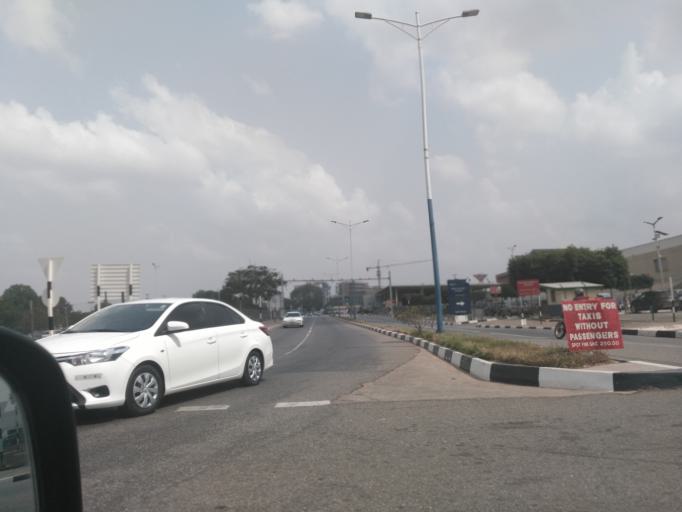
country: GH
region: Greater Accra
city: Accra
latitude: 5.6058
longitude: -0.1731
